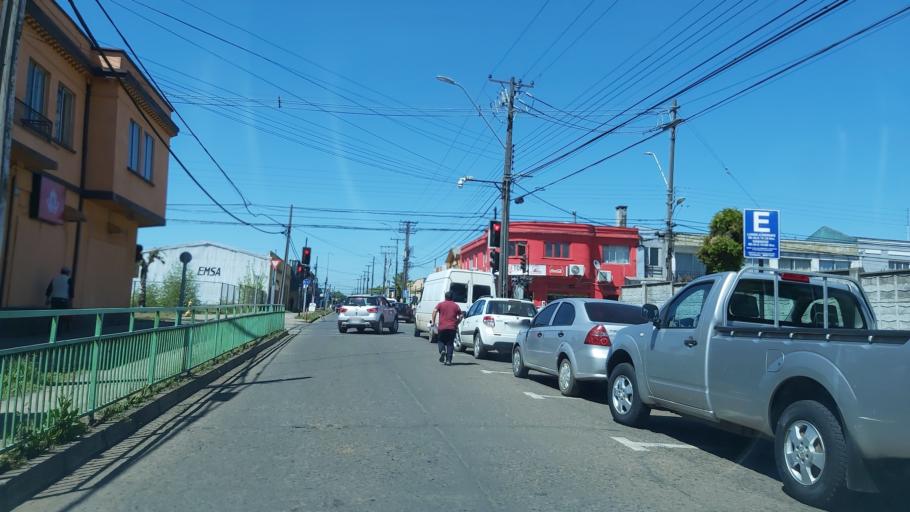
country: CL
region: Araucania
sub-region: Provincia de Malleco
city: Victoria
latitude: -38.2331
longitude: -72.3294
